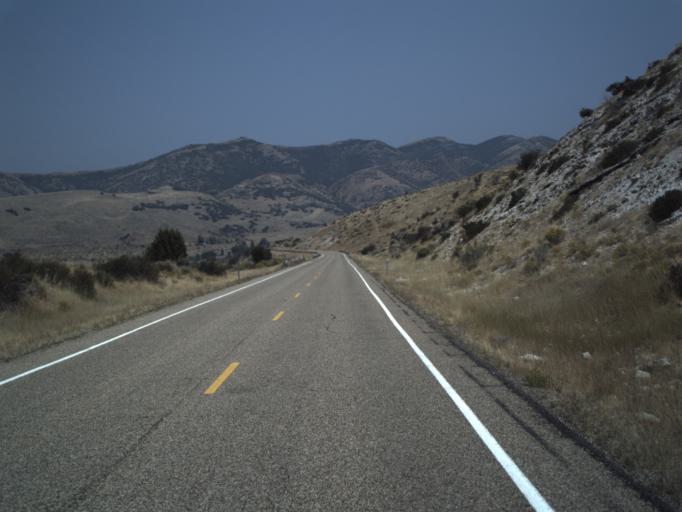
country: US
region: Utah
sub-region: Morgan County
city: Morgan
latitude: 40.9092
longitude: -111.5871
